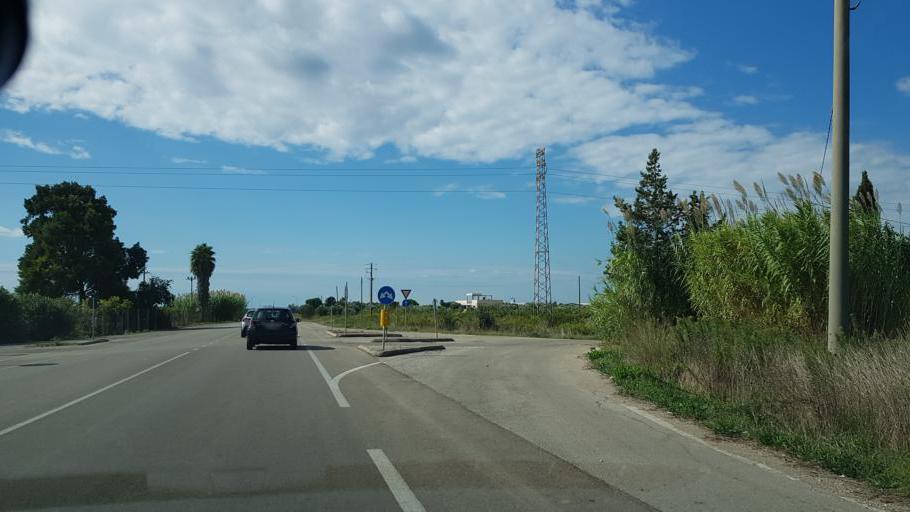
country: IT
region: Apulia
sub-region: Provincia di Lecce
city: Leverano
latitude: 40.3043
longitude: 18.0135
